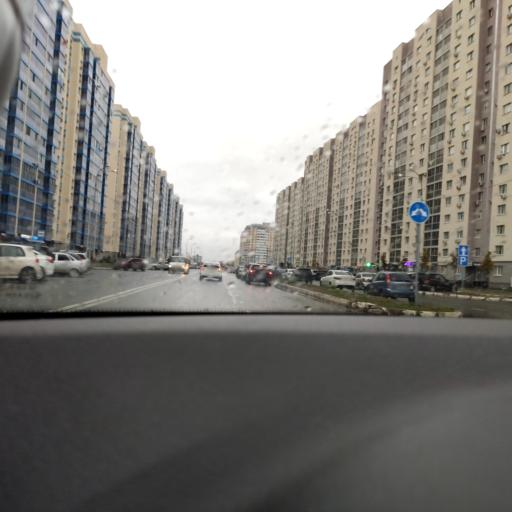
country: RU
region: Samara
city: Rozhdestveno
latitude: 53.1494
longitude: 50.0745
